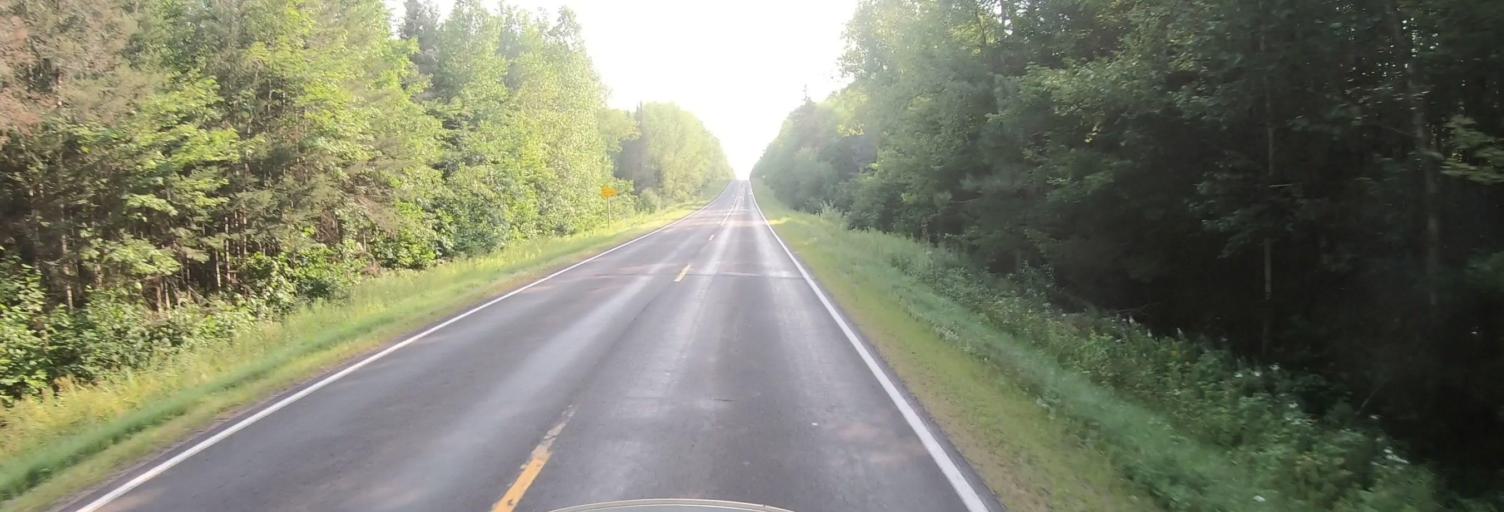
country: US
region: Wisconsin
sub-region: Ashland County
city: Ashland
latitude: 46.1901
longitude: -90.8825
